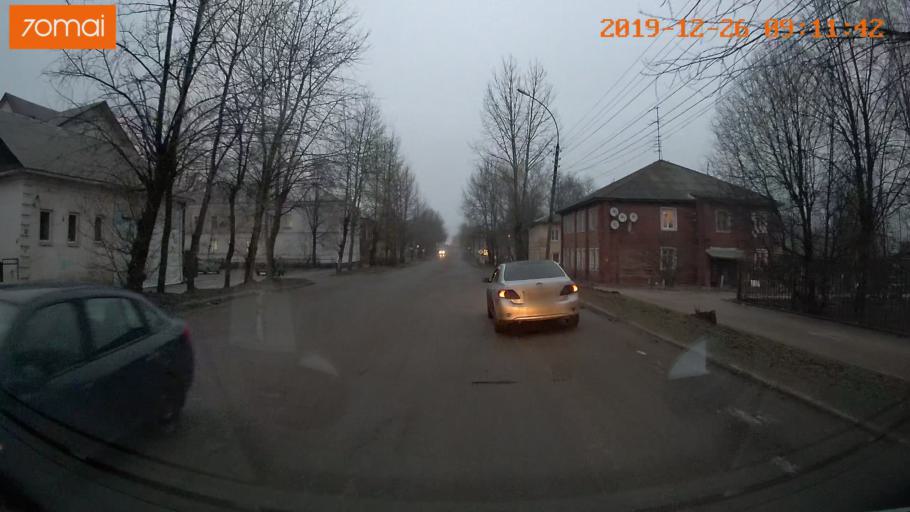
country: RU
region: Vologda
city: Gryazovets
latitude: 58.8774
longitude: 40.2529
